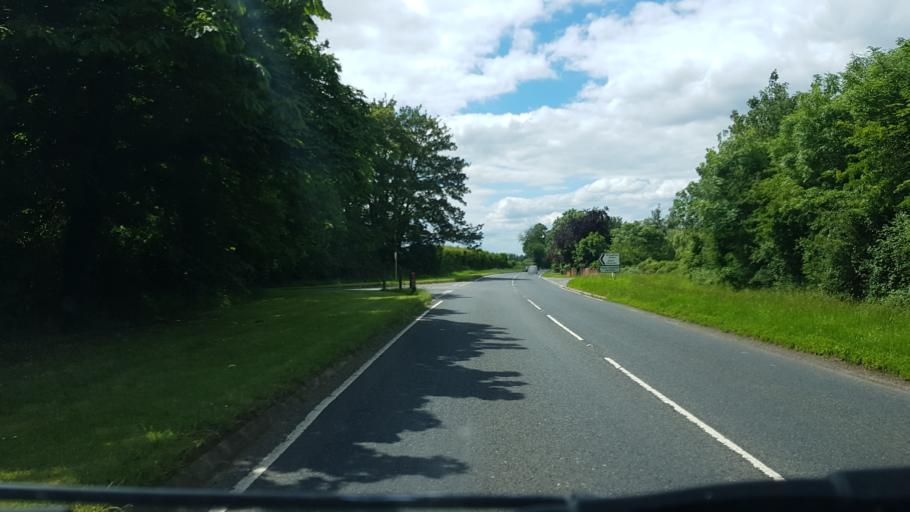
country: GB
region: England
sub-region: Worcestershire
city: Bromsgrove
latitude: 52.2600
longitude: -2.0710
